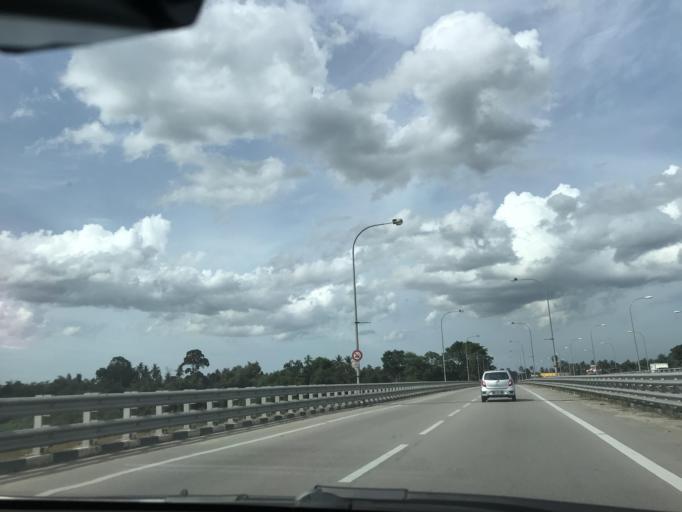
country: MY
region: Kelantan
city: Kampung Lemal
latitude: 6.0314
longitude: 102.1454
